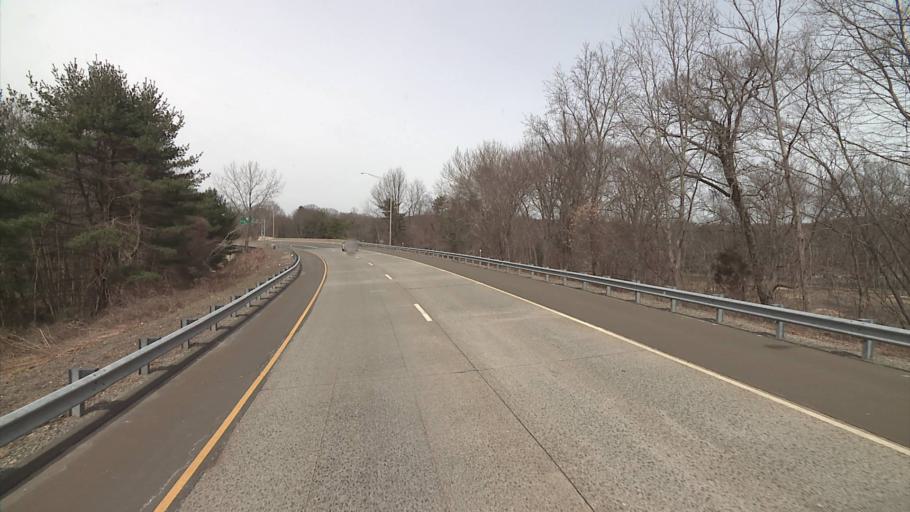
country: US
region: Connecticut
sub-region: Fairfield County
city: Trumbull
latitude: 41.2352
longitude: -73.1865
